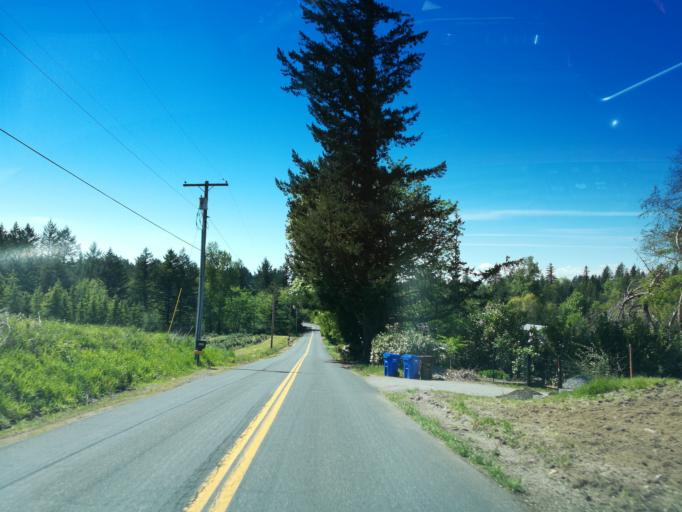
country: US
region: Oregon
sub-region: Multnomah County
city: Troutdale
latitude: 45.5119
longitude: -122.3590
